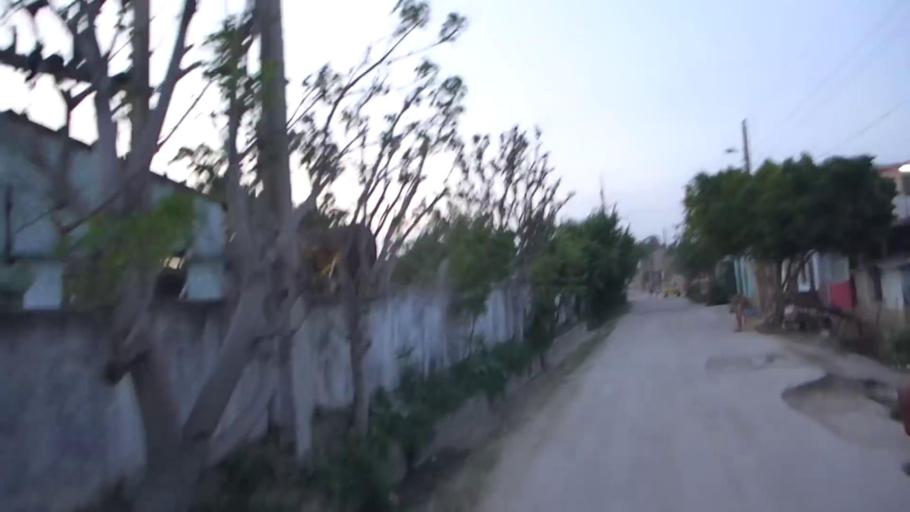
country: CU
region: Camaguey
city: Camaguey
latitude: 21.3732
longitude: -77.9186
